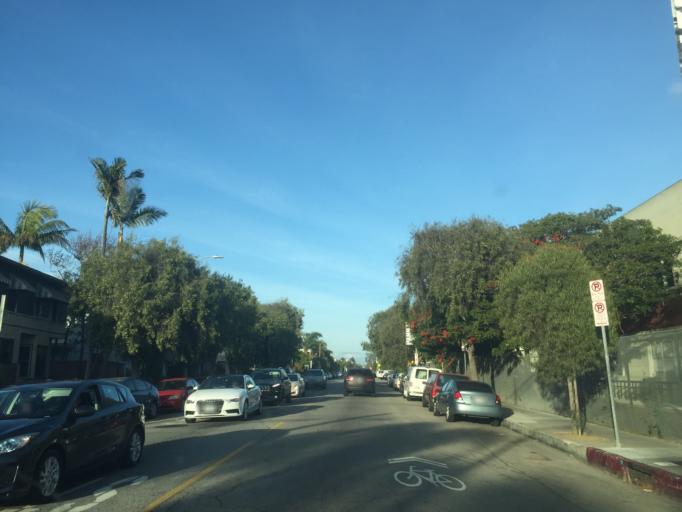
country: US
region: California
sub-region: Los Angeles County
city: Santa Monica
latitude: 33.9965
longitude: -118.4770
